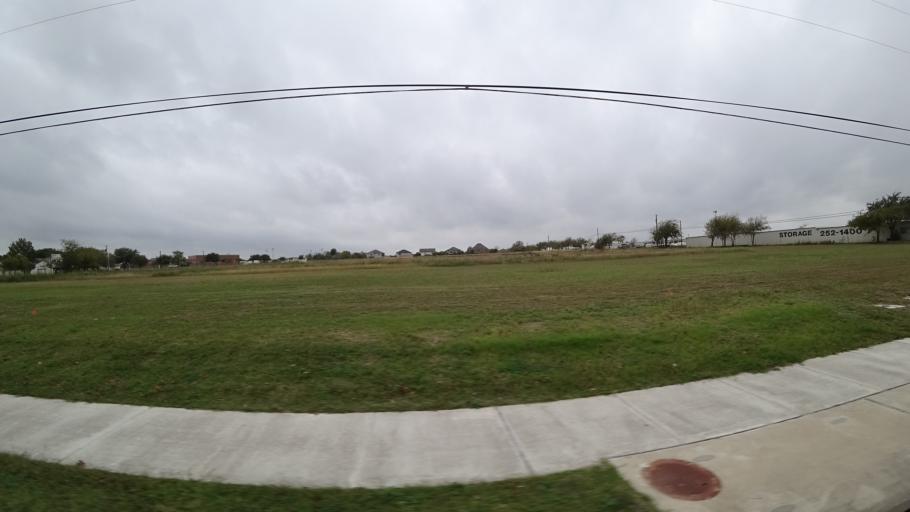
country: US
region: Texas
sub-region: Travis County
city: Pflugerville
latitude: 30.4606
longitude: -97.6193
